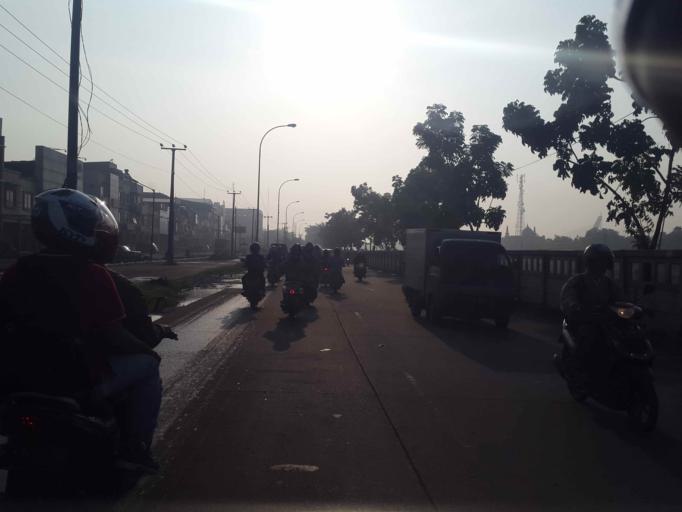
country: ID
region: West Java
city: Bekasi
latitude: -6.2718
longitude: 107.0480
